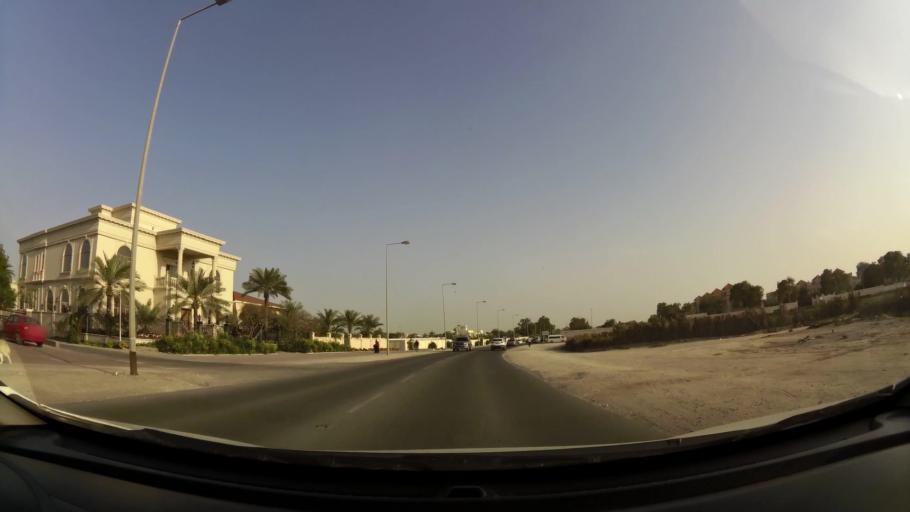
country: BH
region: Manama
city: Jidd Hafs
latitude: 26.2094
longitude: 50.4816
